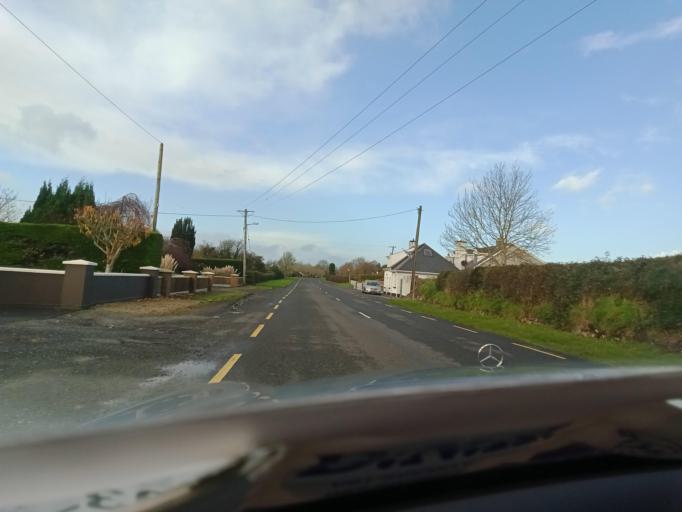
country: IE
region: Munster
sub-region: Waterford
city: Portlaw
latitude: 52.3220
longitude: -7.3045
